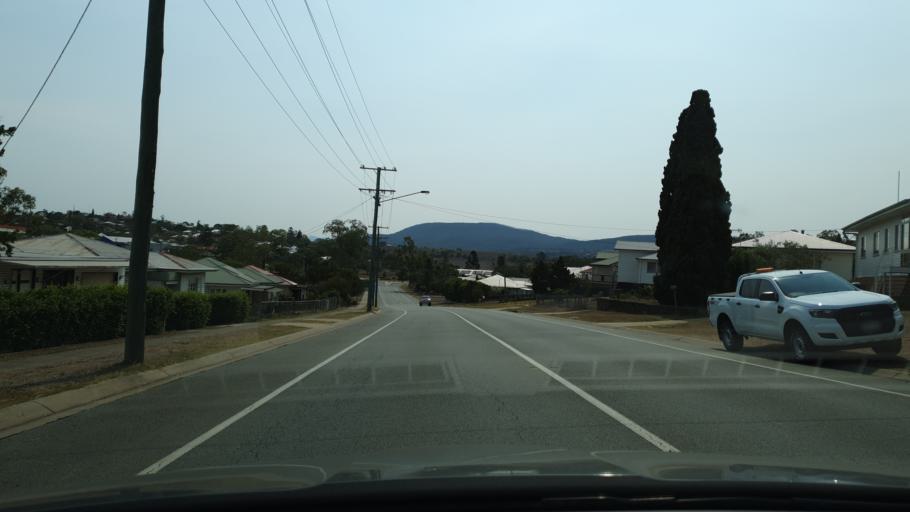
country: AU
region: Queensland
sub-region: Ipswich
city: Deebing Heights
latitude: -27.9927
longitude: 152.6865
